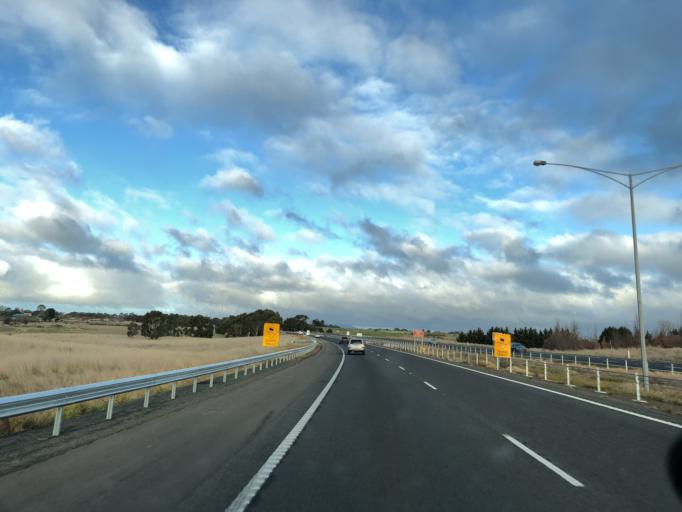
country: AU
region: Victoria
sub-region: Mount Alexander
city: Castlemaine
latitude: -37.2201
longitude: 144.4169
